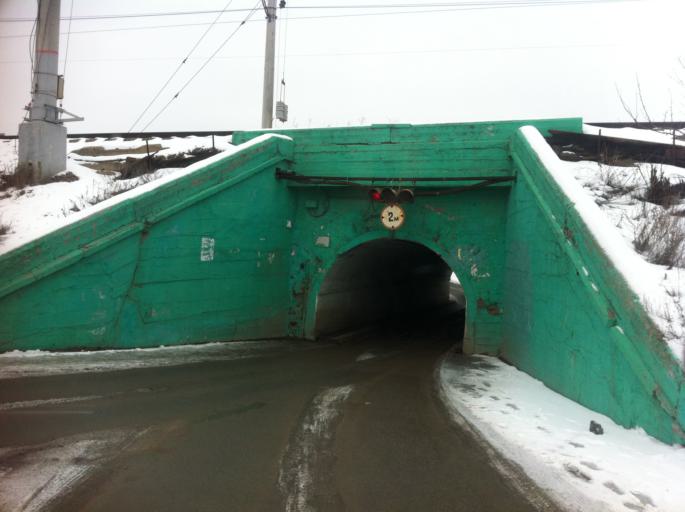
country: RU
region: St.-Petersburg
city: Uritsk
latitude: 59.8238
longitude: 30.1657
